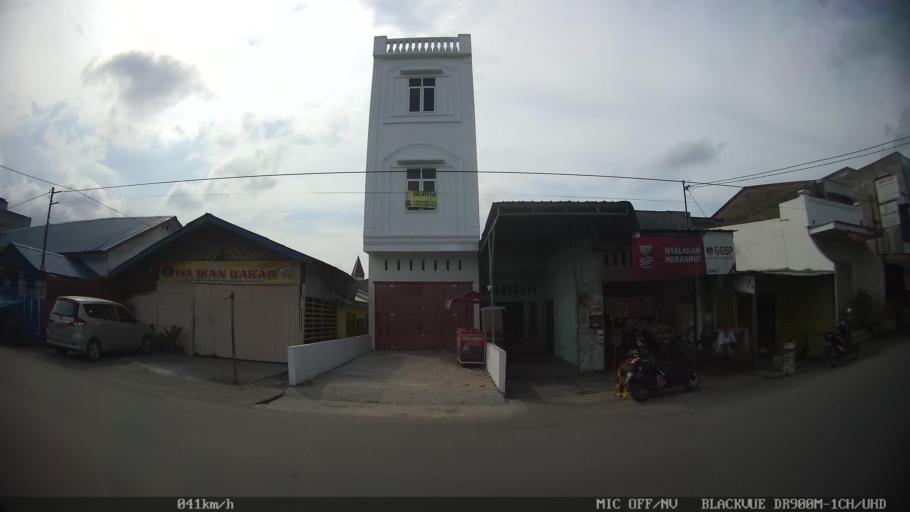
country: ID
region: North Sumatra
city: Medan
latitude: 3.5994
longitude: 98.7563
